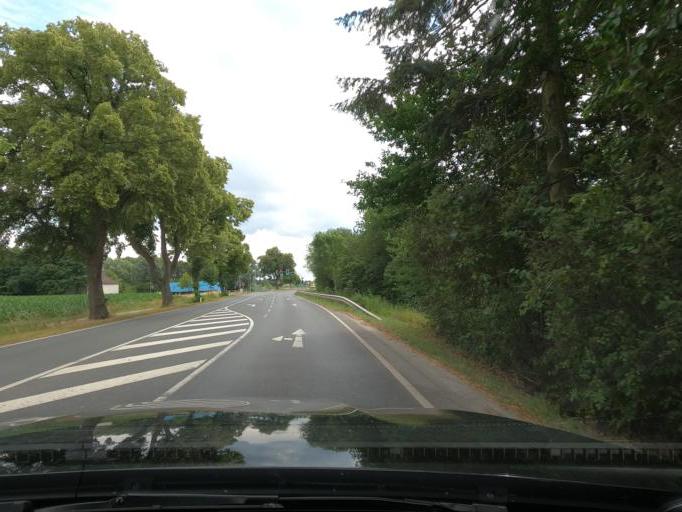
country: DE
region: Lower Saxony
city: Sehnde
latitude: 52.3324
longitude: 9.9477
